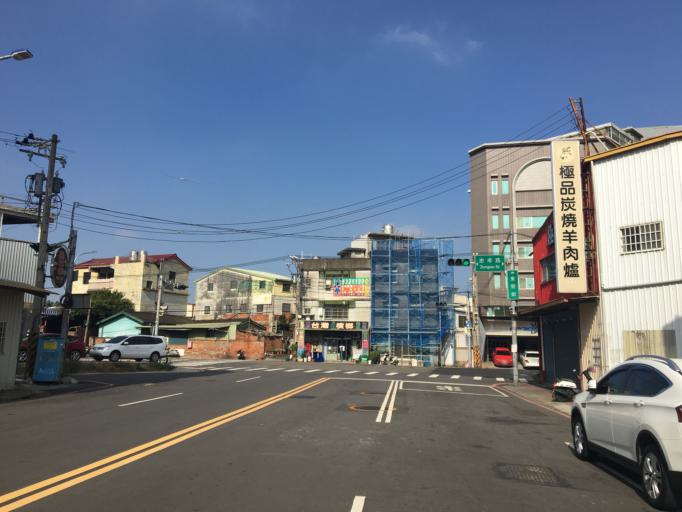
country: TW
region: Taiwan
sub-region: Hsinchu
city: Hsinchu
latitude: 24.8043
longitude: 120.9899
